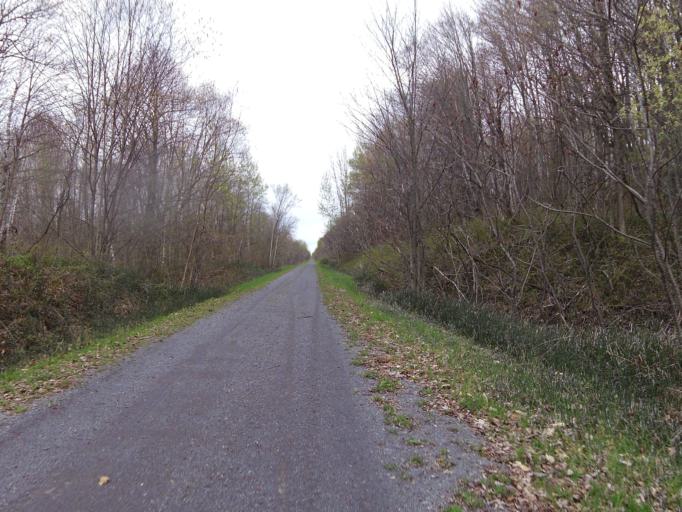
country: CA
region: Quebec
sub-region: Outaouais
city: Papineauville
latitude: 45.5169
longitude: -74.9431
